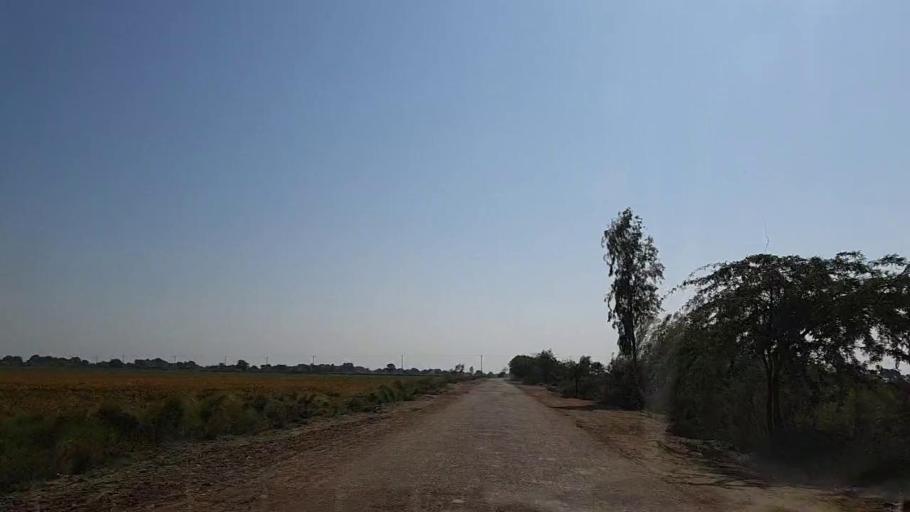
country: PK
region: Sindh
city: Chuhar Jamali
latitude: 24.5230
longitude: 68.0913
